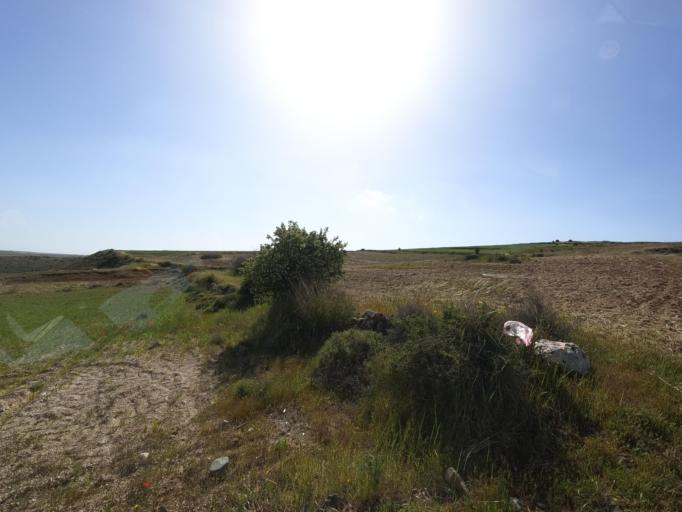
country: CY
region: Lefkosia
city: Astromeritis
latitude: 35.0873
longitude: 33.0216
